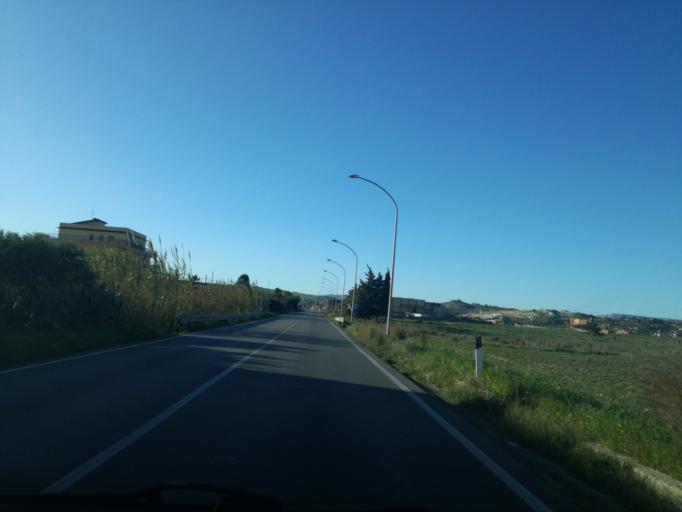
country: IT
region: Sicily
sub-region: Provincia di Caltanissetta
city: Gela
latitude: 37.0948
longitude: 14.1750
